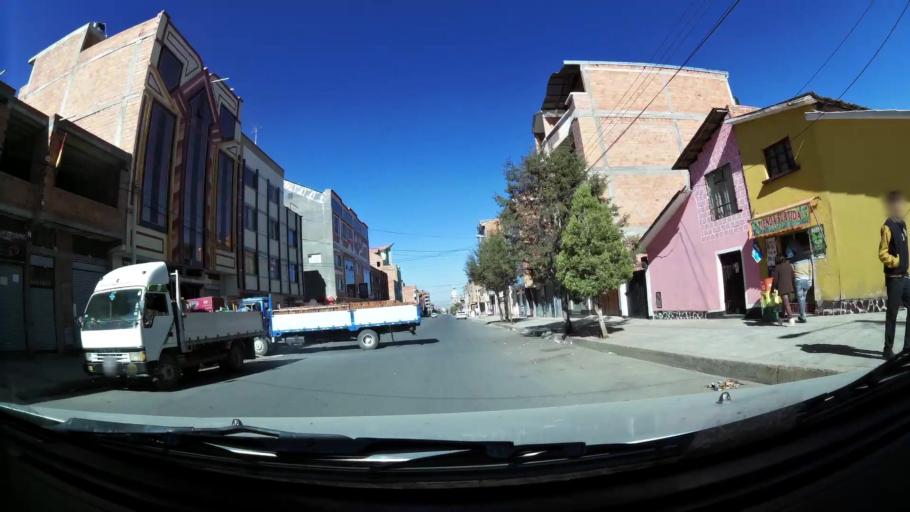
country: BO
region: La Paz
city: La Paz
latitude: -16.5219
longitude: -68.2051
